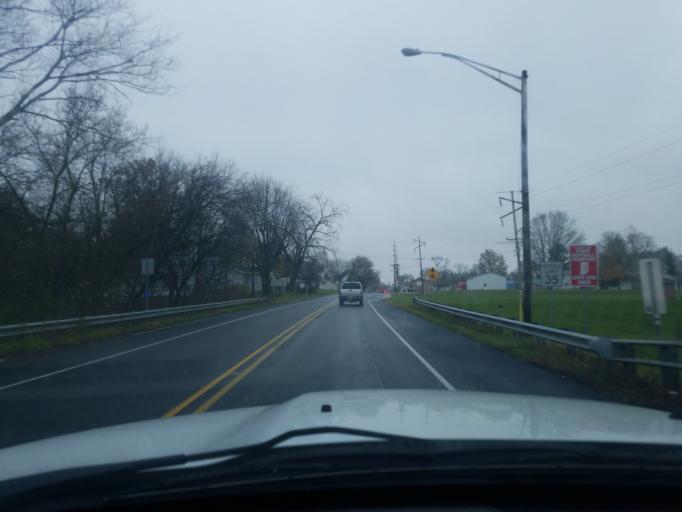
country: US
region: Indiana
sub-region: Cass County
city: Galveston
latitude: 40.5816
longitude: -86.1900
